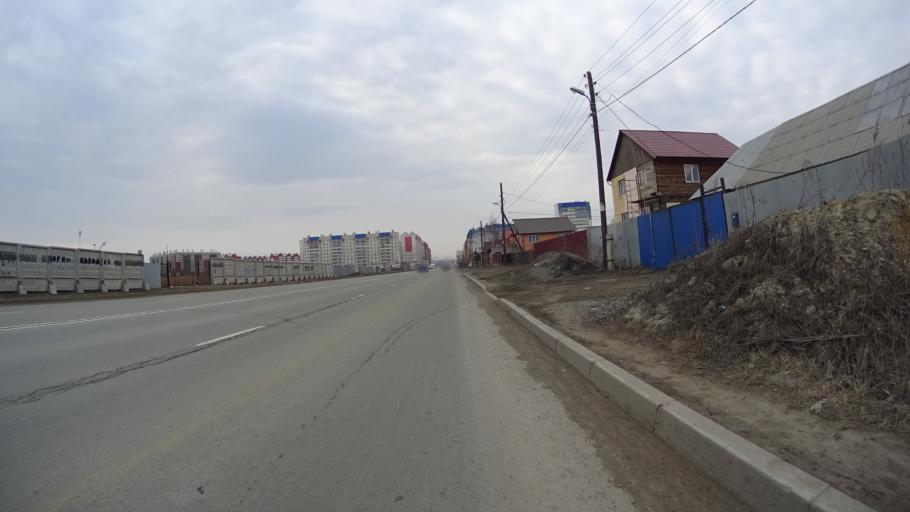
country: RU
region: Chelyabinsk
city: Zheleznodorozhnyy
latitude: 55.1627
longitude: 61.5228
